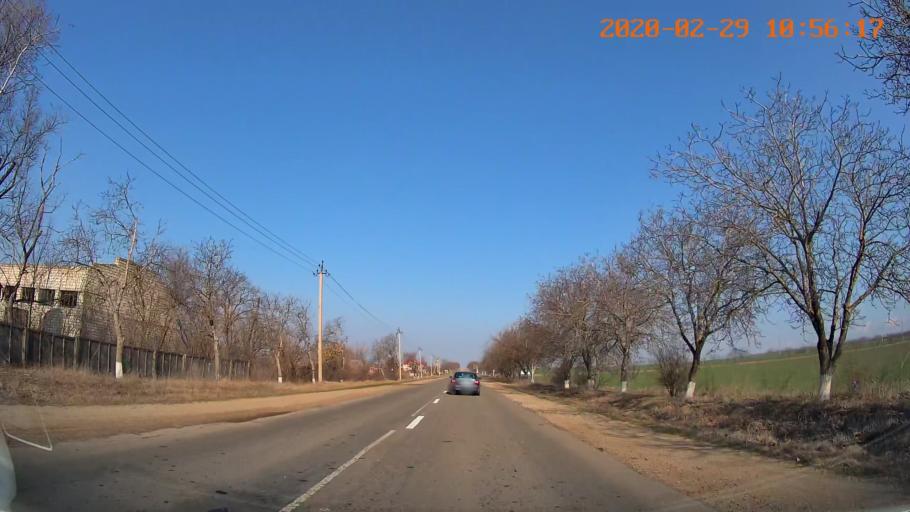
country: MD
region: Telenesti
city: Grigoriopol
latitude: 47.1440
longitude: 29.3250
